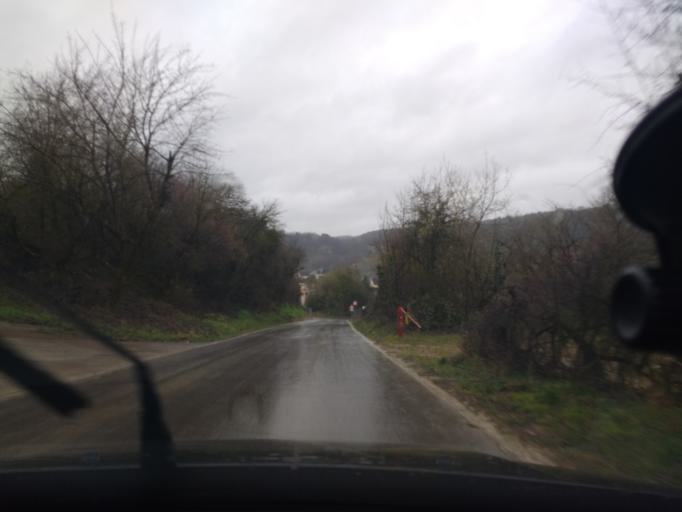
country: DE
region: Rheinland-Pfalz
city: Wellen
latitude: 49.6686
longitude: 6.4396
